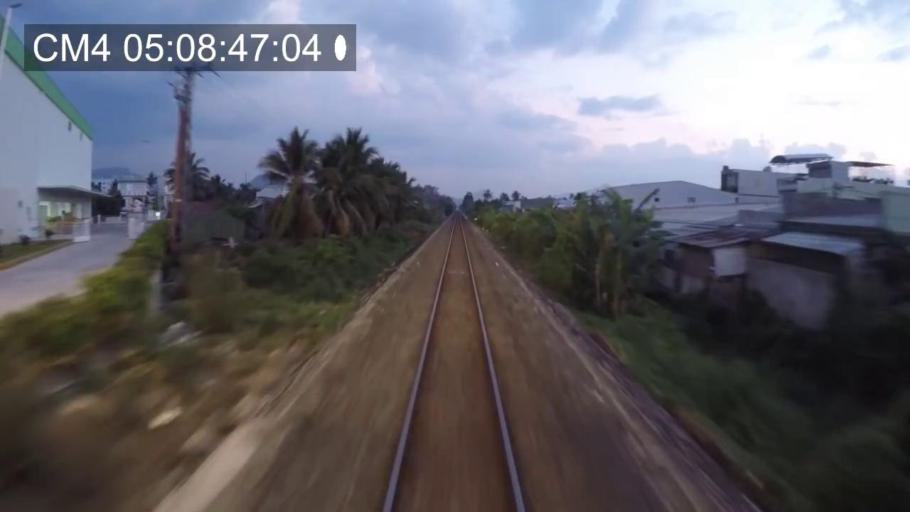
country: VN
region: Khanh Hoa
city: Nha Trang
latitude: 12.2954
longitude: 109.1864
